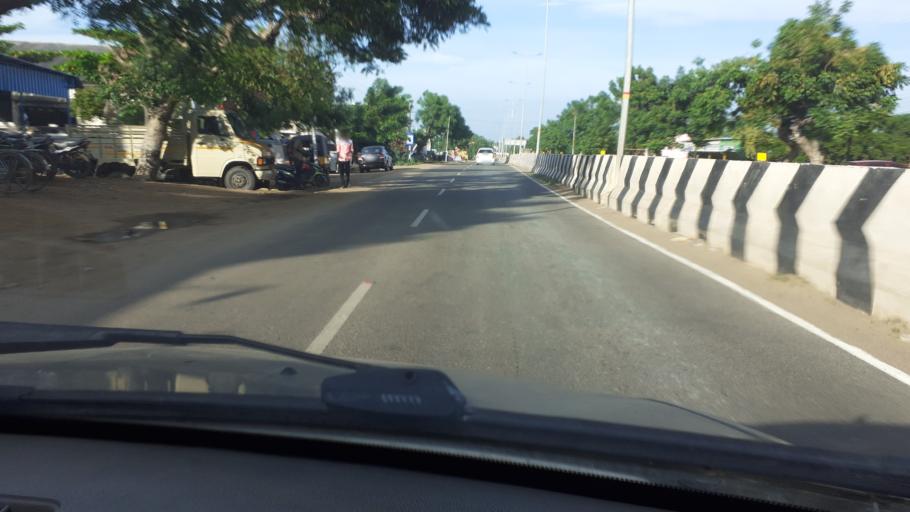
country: IN
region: Tamil Nadu
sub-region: Tirunelveli Kattabo
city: Tirunelveli
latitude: 8.6734
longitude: 77.7195
